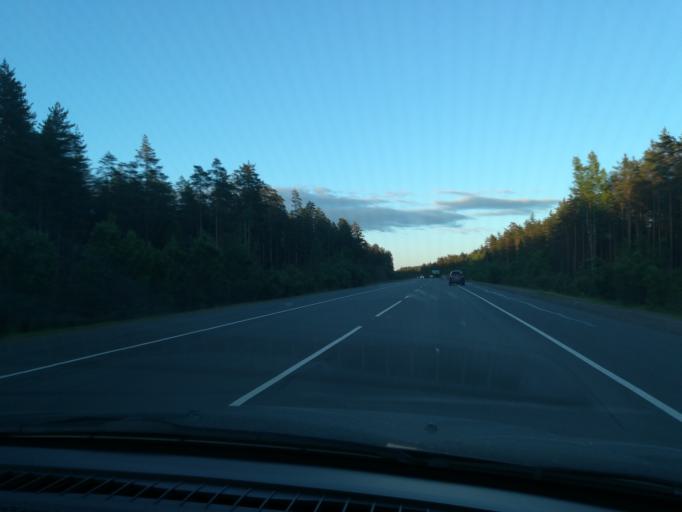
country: RU
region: Leningrad
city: Yakovlevo
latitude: 60.3608
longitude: 29.5755
